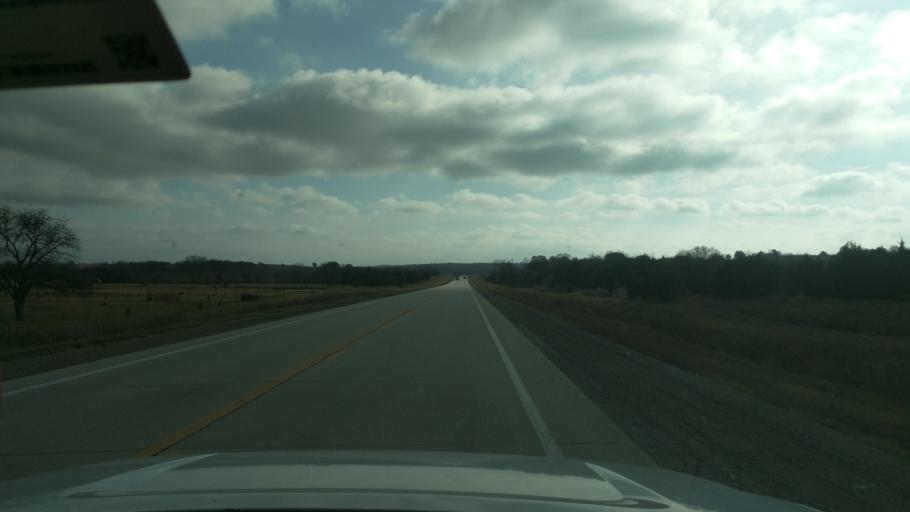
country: US
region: Kansas
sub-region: Chautauqua County
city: Sedan
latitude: 37.0746
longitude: -96.0794
